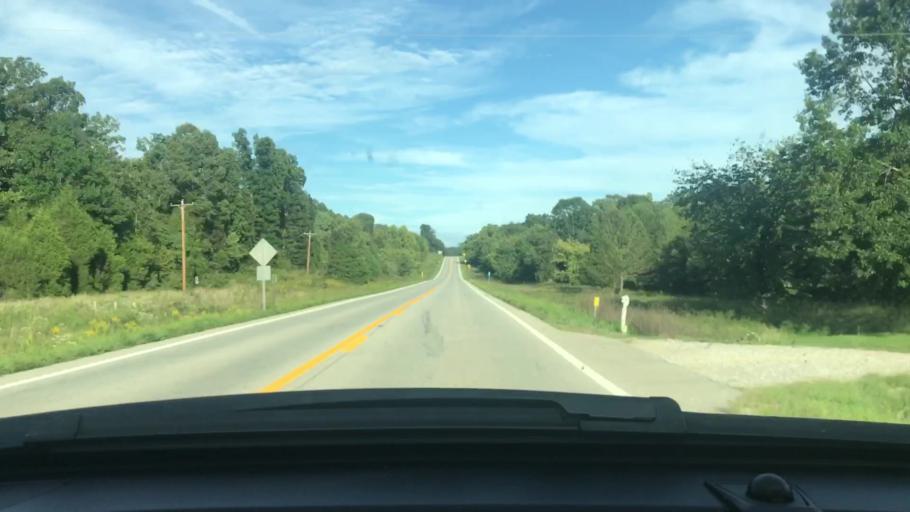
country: US
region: Arkansas
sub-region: Sharp County
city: Cherokee Village
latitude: 36.2746
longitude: -91.3484
